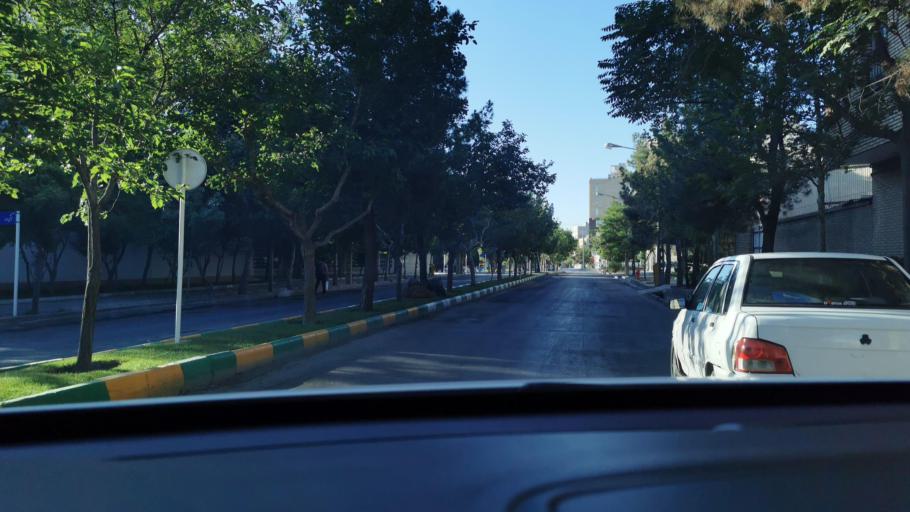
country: IR
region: Razavi Khorasan
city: Mashhad
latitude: 36.3597
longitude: 59.4905
